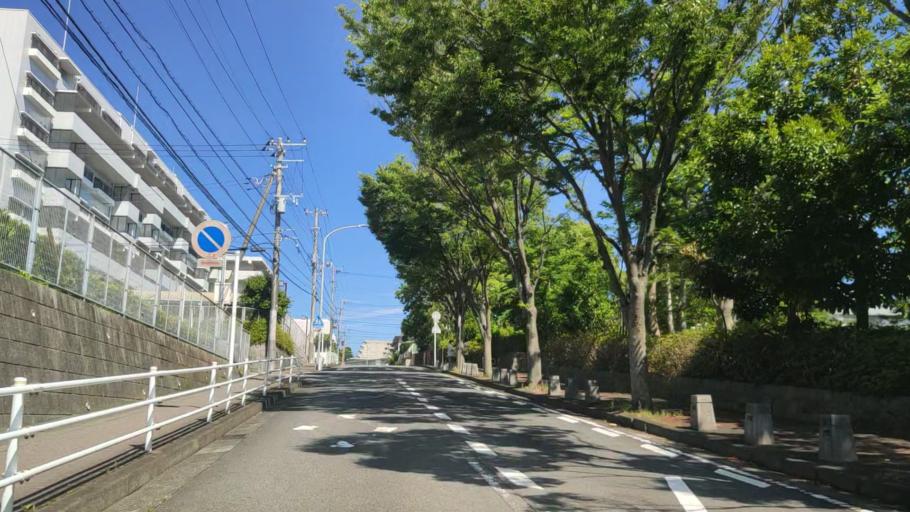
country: JP
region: Kanagawa
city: Fujisawa
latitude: 35.3848
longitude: 139.5222
